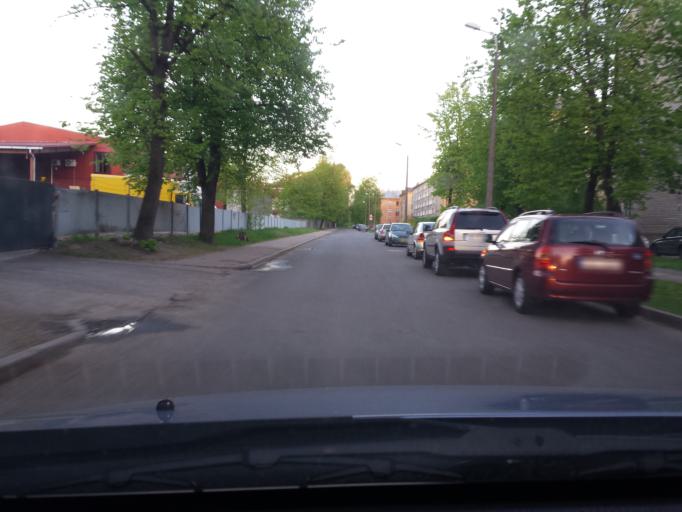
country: LV
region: Riga
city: Riga
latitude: 56.9905
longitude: 24.1337
